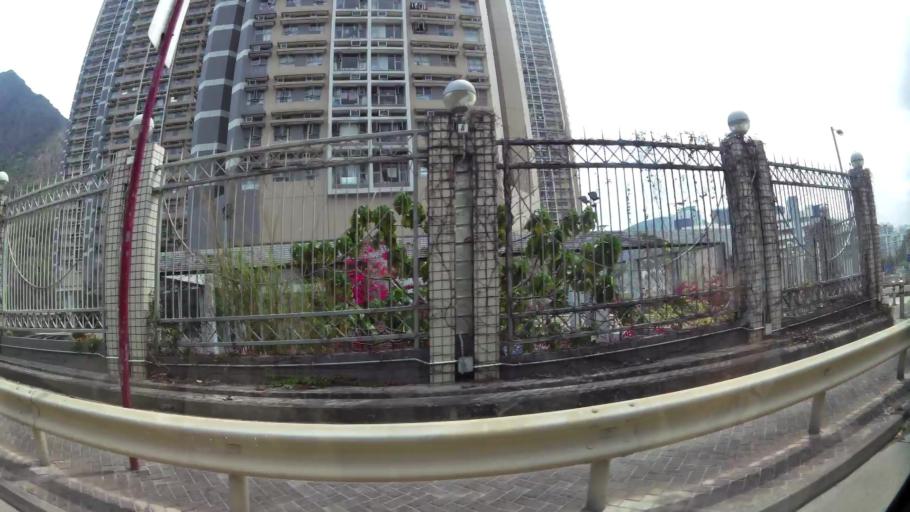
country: HK
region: Kowloon City
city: Kowloon
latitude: 22.3319
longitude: 114.2208
